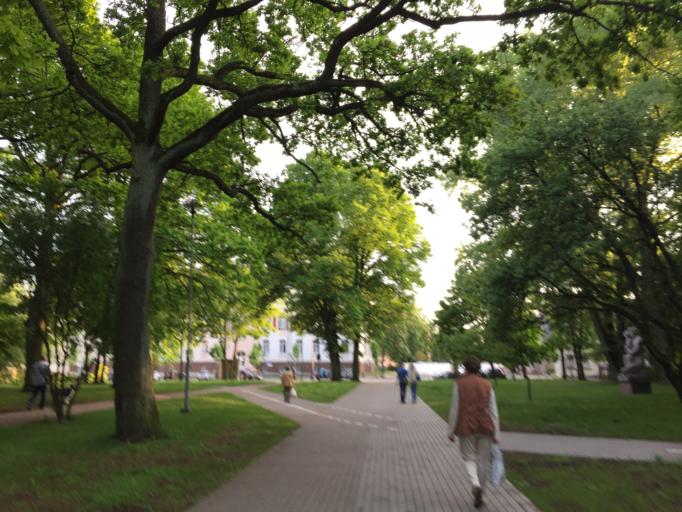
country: LT
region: Klaipedos apskritis
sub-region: Klaipeda
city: Klaipeda
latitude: 55.7158
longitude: 21.1368
